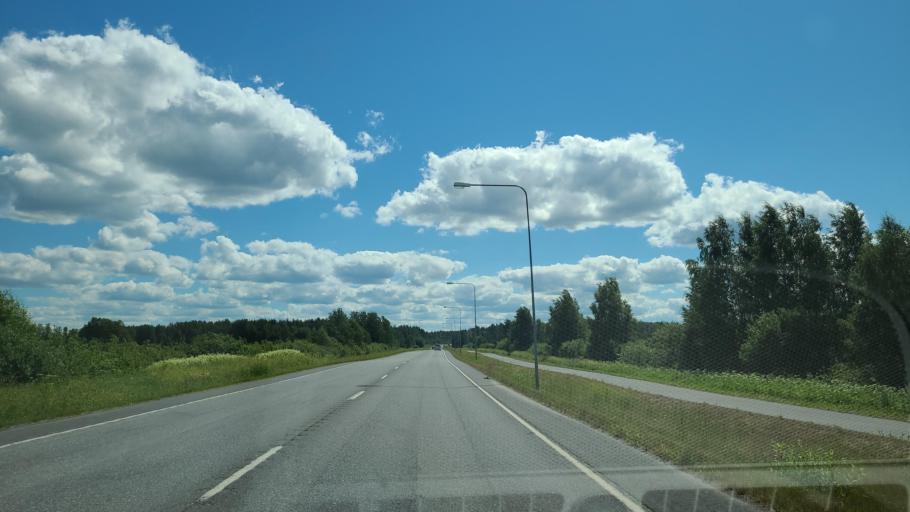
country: FI
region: Southern Ostrobothnia
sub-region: Seinaejoki
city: Seinaejoki
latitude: 62.8493
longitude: 22.7860
